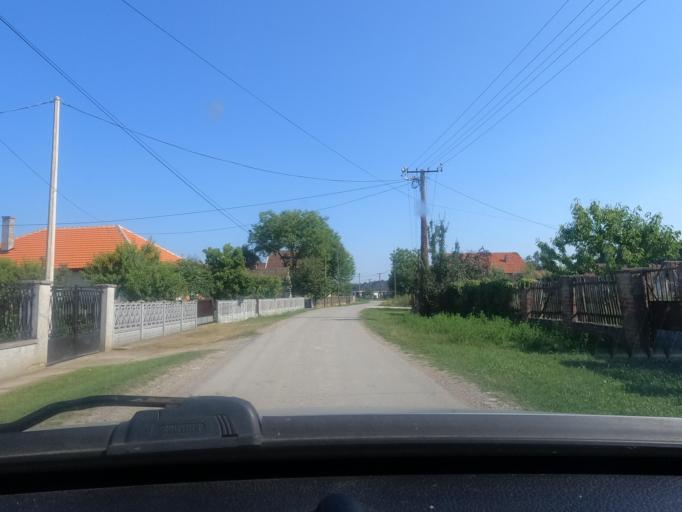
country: RS
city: Bogosavac
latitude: 44.7501
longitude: 19.5817
